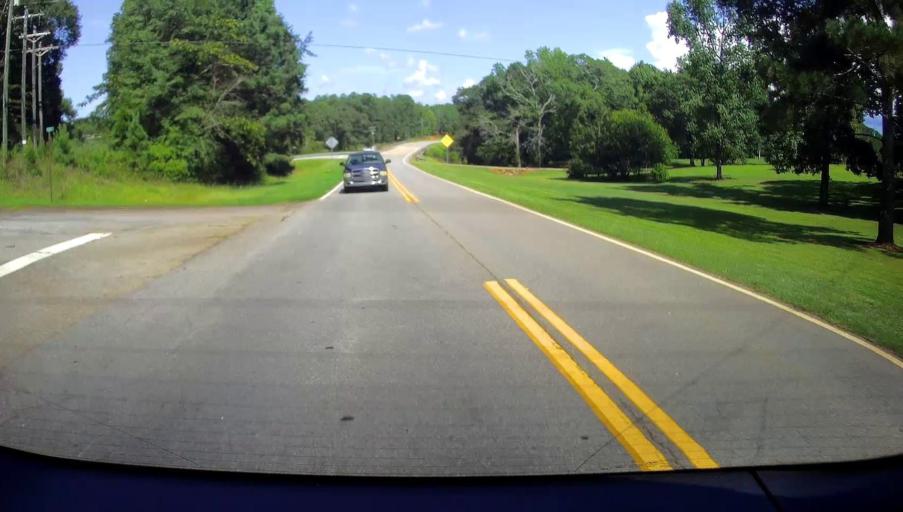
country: US
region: Georgia
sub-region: Upson County
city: Hannahs Mill
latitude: 32.9524
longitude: -84.3059
